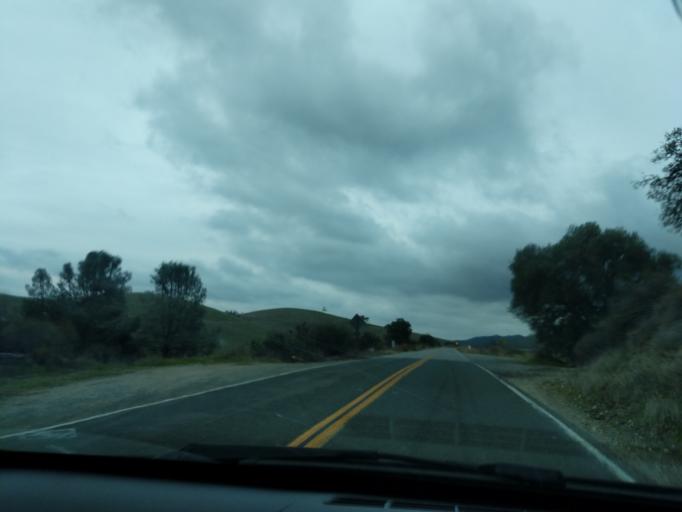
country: US
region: California
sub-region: Monterey County
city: Soledad
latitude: 36.5758
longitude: -121.1863
